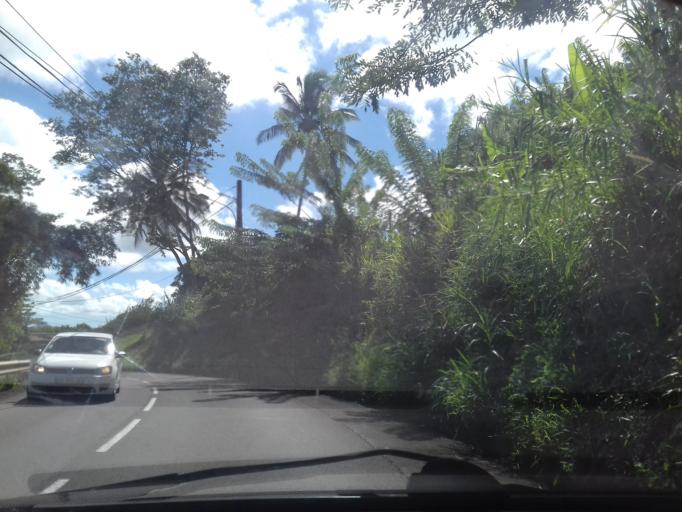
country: MQ
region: Martinique
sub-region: Martinique
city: Saint-Joseph
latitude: 14.6661
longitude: -61.0479
